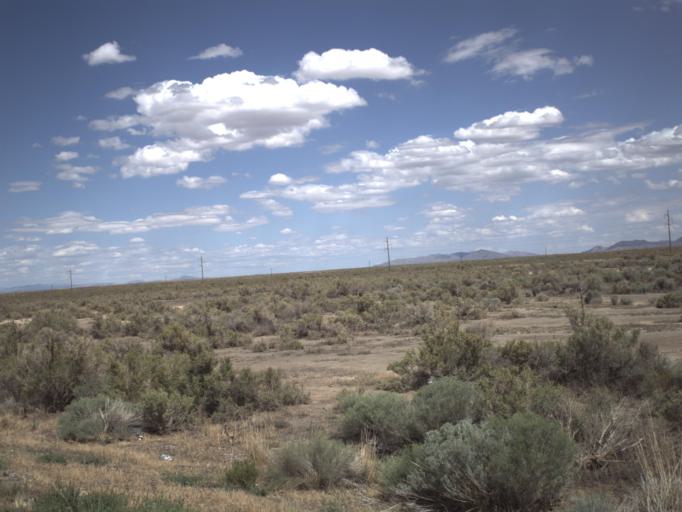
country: US
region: Utah
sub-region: Millard County
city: Delta
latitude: 39.2785
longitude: -112.4588
